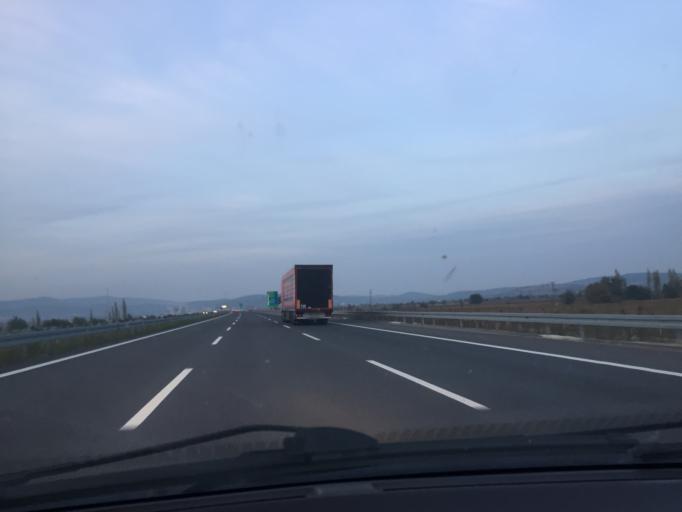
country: TR
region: Manisa
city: Halitpasa
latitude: 38.7527
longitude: 27.6601
